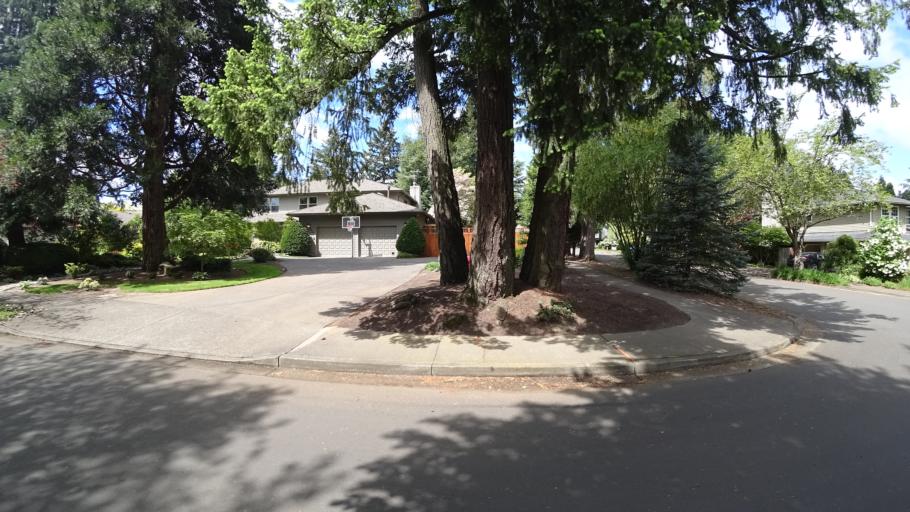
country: US
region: Oregon
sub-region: Washington County
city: Beaverton
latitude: 45.4648
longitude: -122.8119
